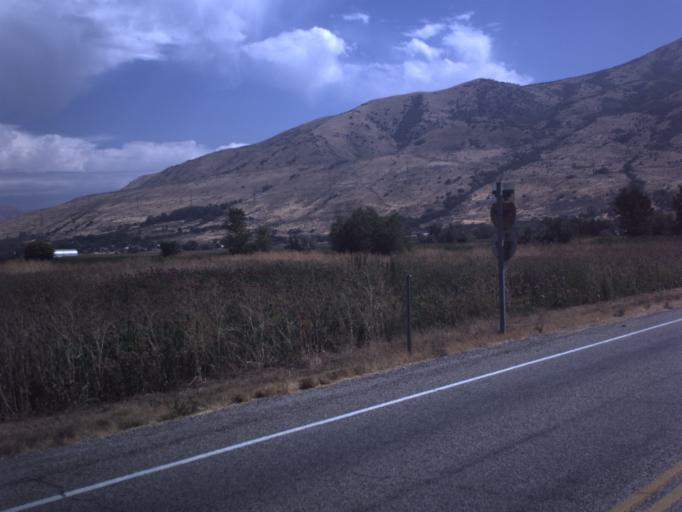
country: US
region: Utah
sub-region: Box Elder County
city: Willard
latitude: 41.4225
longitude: -112.0491
